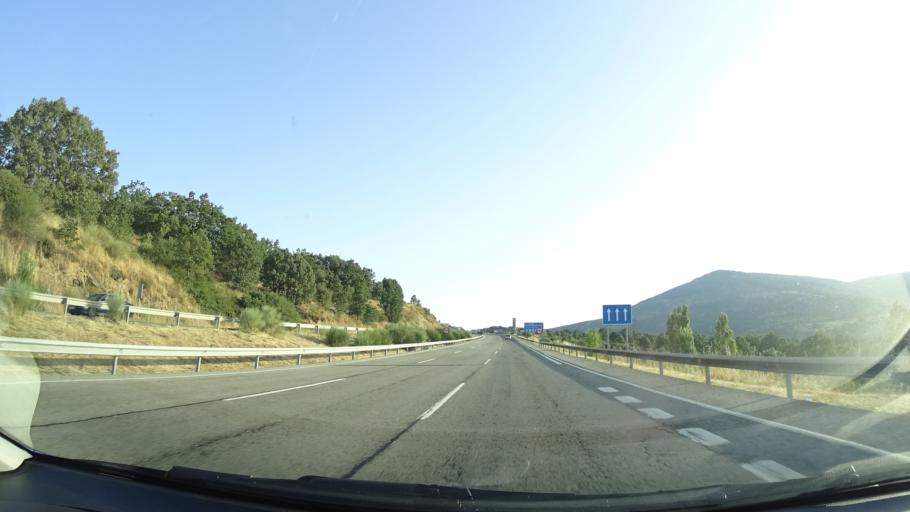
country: ES
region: Madrid
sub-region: Provincia de Madrid
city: Robregordo
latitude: 41.0860
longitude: -3.5960
